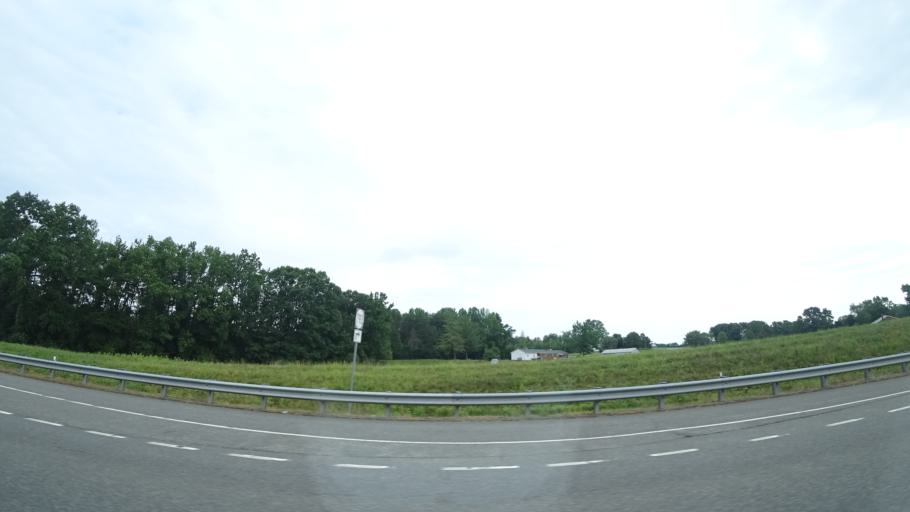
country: US
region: Virginia
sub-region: Spotsylvania County
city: Spotsylvania Courthouse
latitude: 38.1603
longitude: -77.6680
